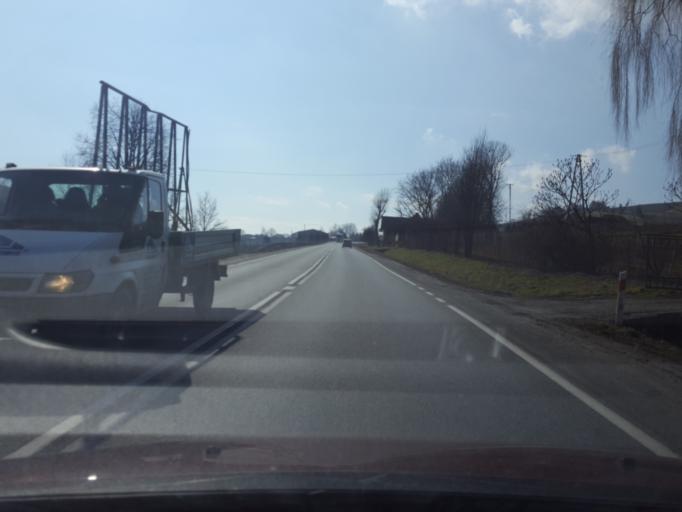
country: PL
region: Lesser Poland Voivodeship
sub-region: Powiat nowosadecki
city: Lososina Dolna
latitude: 49.7327
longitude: 20.6378
